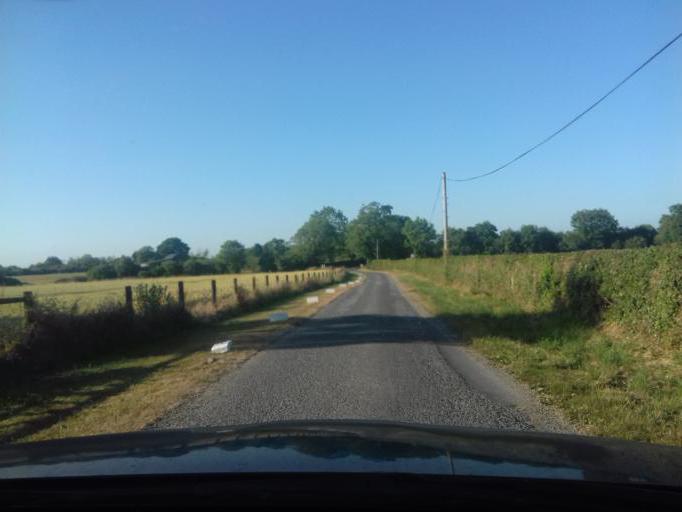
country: IE
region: Leinster
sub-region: Fingal County
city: Blanchardstown
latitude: 53.4501
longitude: -6.3807
